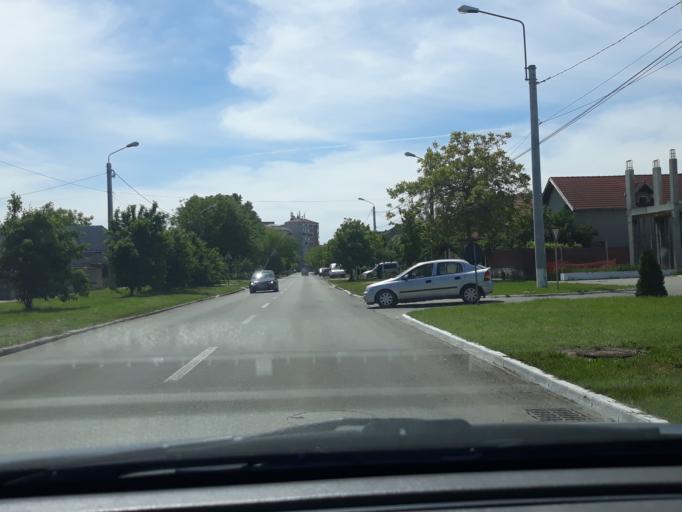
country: RO
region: Bihor
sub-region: Comuna Biharea
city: Oradea
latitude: 47.0574
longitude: 21.9064
